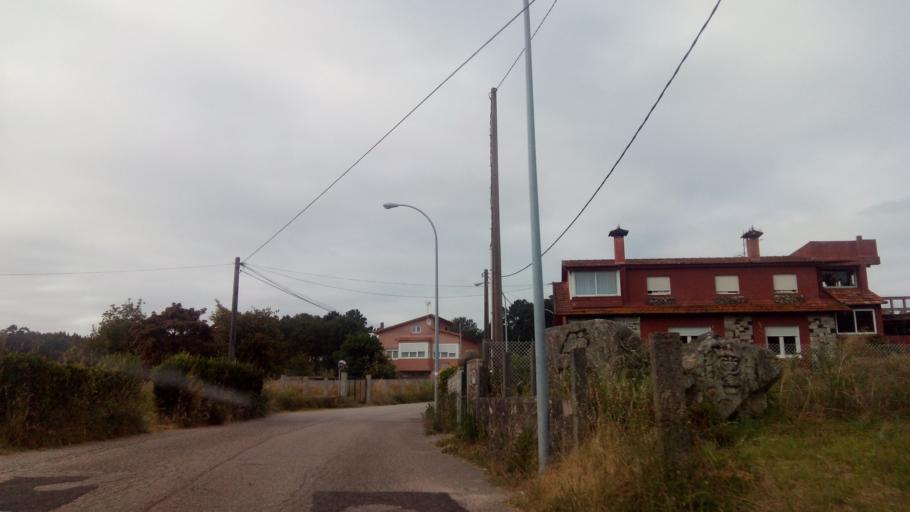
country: ES
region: Galicia
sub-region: Provincia de Pontevedra
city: Nigran
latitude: 42.1170
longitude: -8.8013
